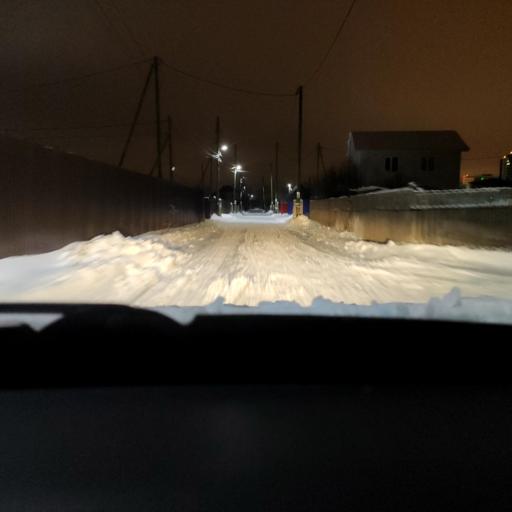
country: RU
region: Perm
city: Kondratovo
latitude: 57.9874
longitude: 56.1062
